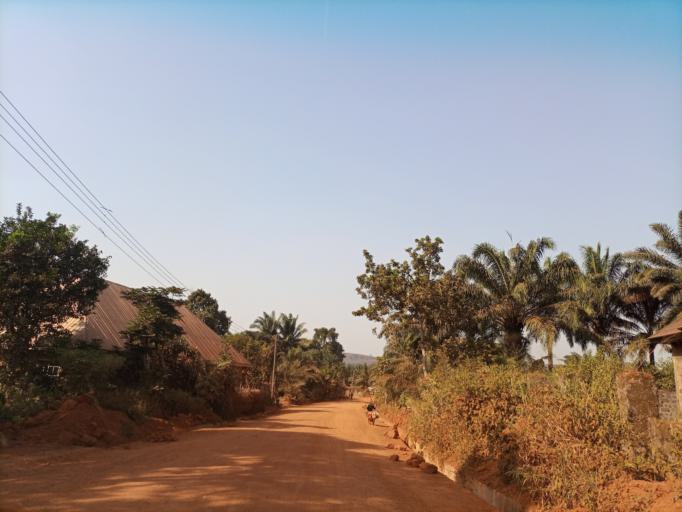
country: NG
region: Enugu
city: Aku
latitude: 6.6959
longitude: 7.3264
